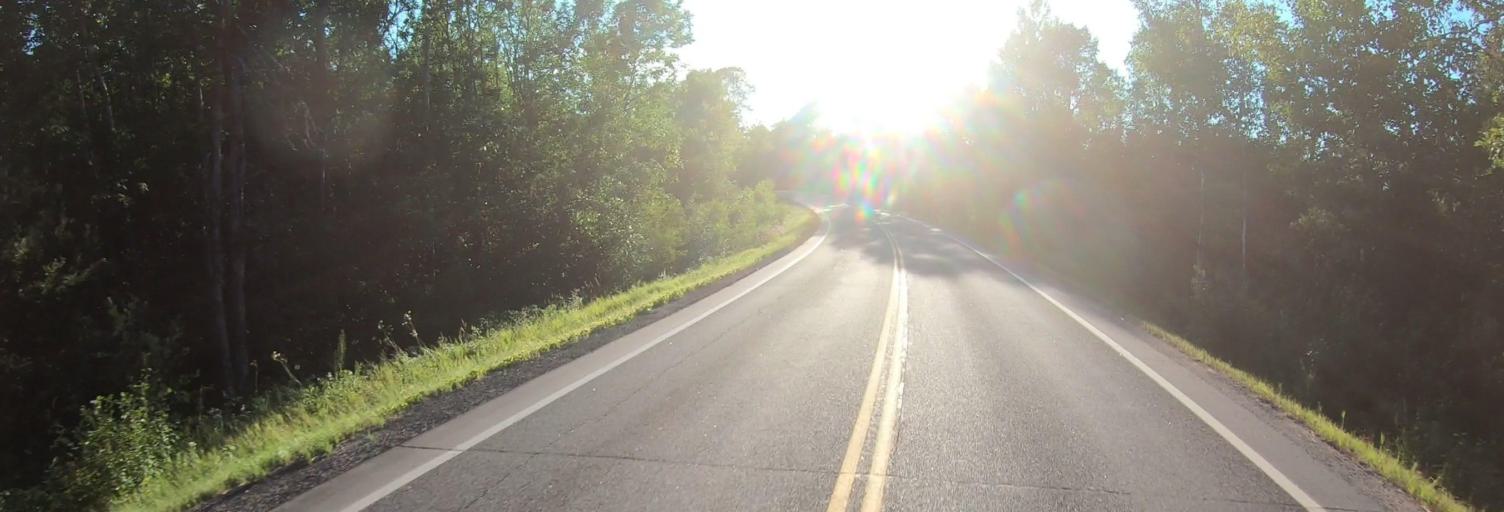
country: US
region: Minnesota
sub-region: Saint Louis County
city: Ely
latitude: 47.9586
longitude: -91.6217
